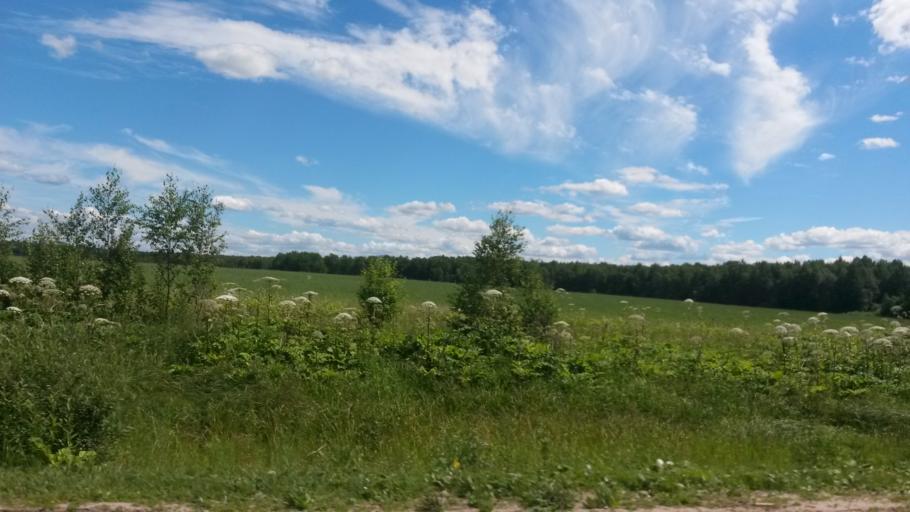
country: RU
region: Ivanovo
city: Rodniki
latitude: 57.1200
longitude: 41.7907
